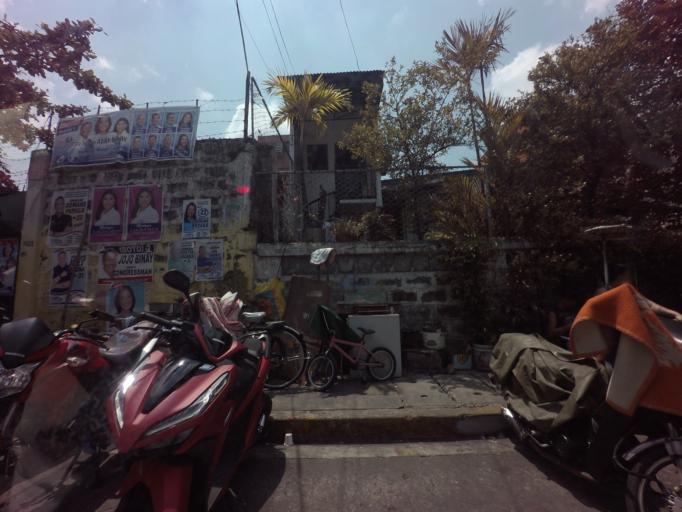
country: PH
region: Metro Manila
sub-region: Mandaluyong
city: Mandaluyong City
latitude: 14.5731
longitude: 121.0241
